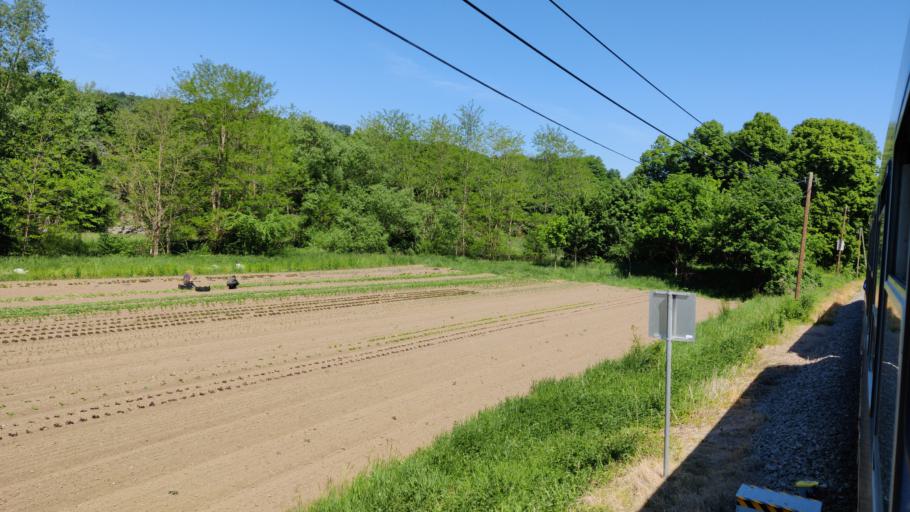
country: AT
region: Lower Austria
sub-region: Politischer Bezirk Horn
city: Gars am Kamp
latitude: 48.5586
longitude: 15.6729
